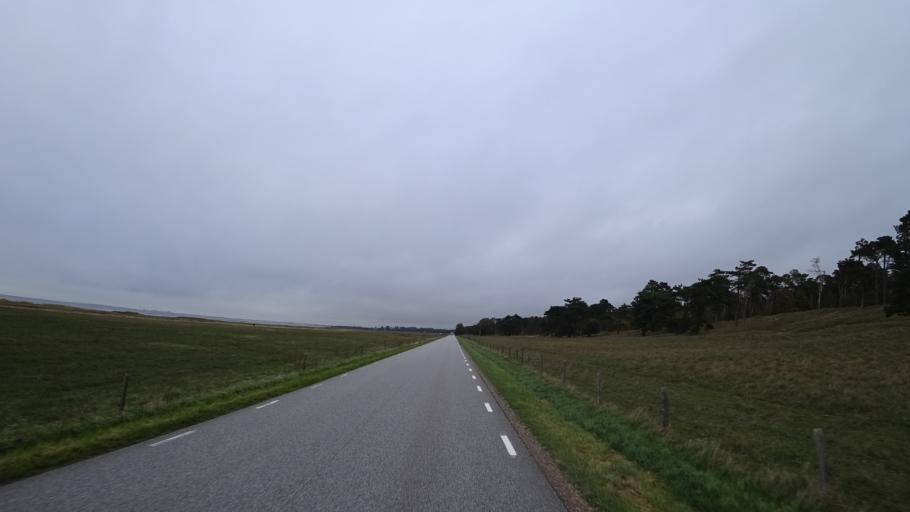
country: SE
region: Skane
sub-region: Kavlinge Kommun
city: Hofterup
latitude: 55.7991
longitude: 12.9376
